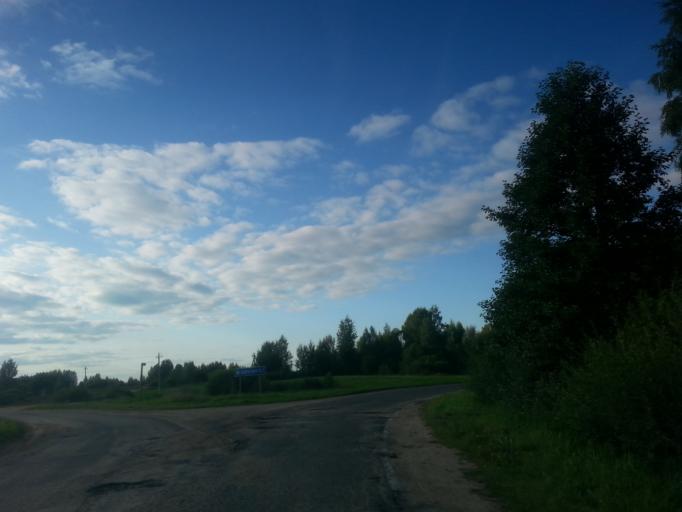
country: BY
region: Minsk
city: Narach
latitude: 54.9690
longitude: 26.6368
